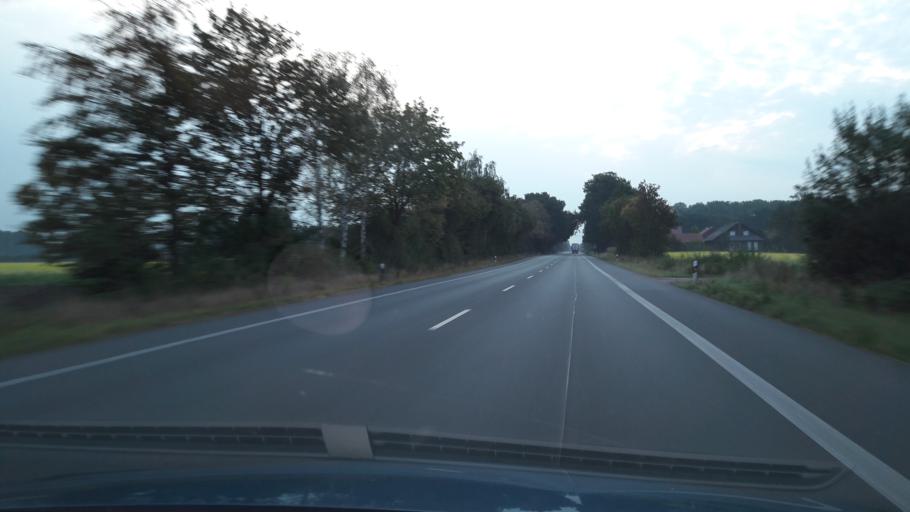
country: DE
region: North Rhine-Westphalia
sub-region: Regierungsbezirk Munster
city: Telgte
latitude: 51.9281
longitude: 7.7628
